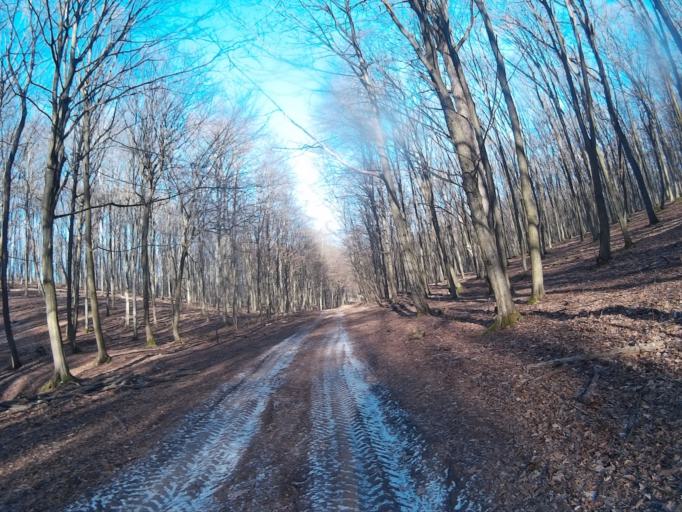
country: HU
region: Borsod-Abauj-Zemplen
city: Rudabanya
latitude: 48.5086
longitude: 20.6060
